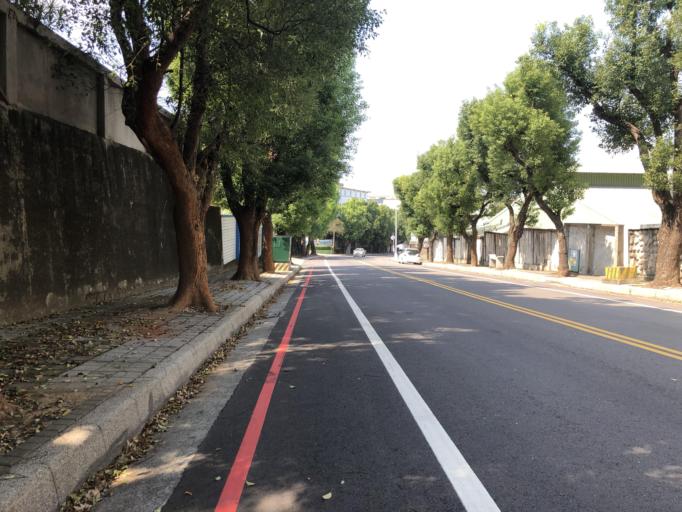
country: TW
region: Taiwan
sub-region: Miaoli
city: Miaoli
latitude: 24.4783
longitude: 120.7931
